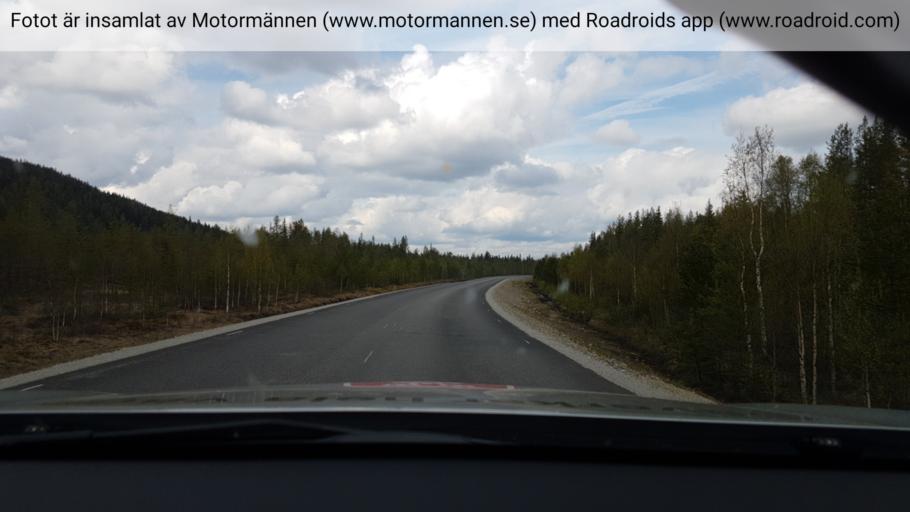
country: SE
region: Vaesterbotten
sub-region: Lycksele Kommun
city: Lycksele
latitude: 64.0280
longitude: 18.4436
